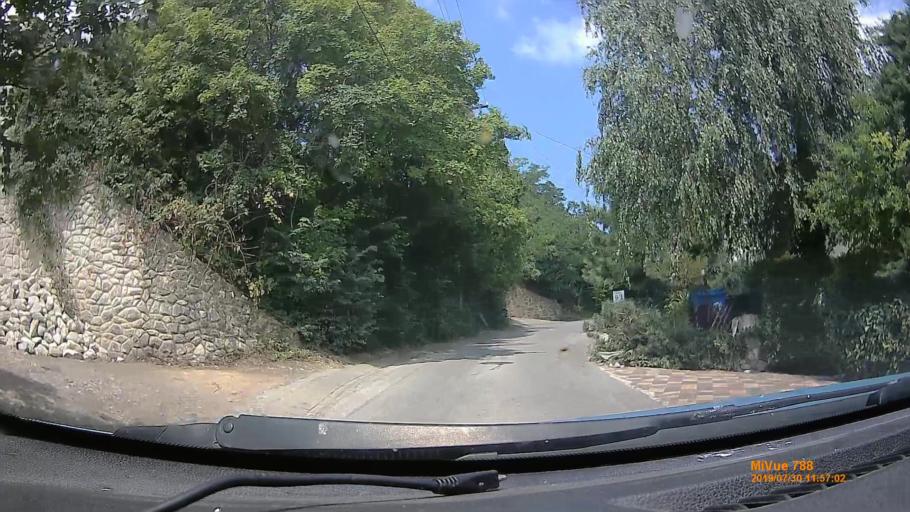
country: HU
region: Baranya
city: Pecs
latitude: 46.0857
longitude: 18.2181
